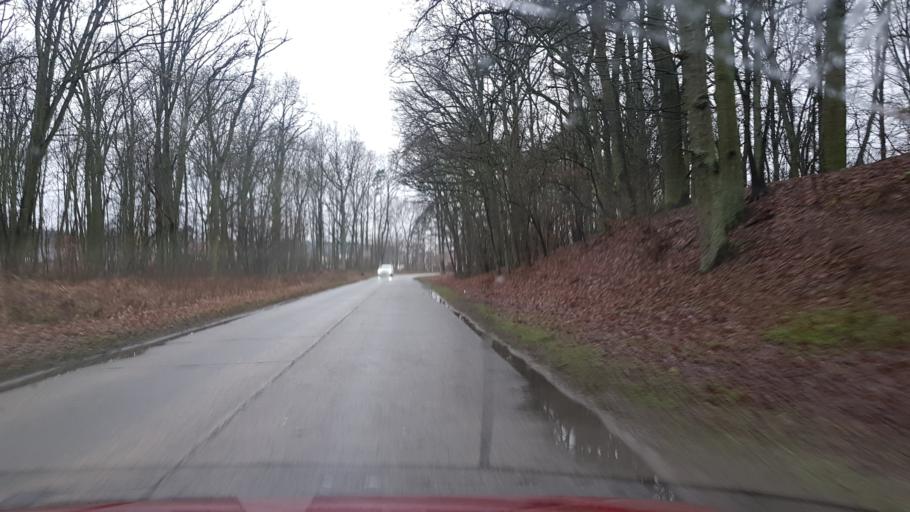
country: PL
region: West Pomeranian Voivodeship
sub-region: Powiat policki
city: Dobra
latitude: 53.5397
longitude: 14.4719
